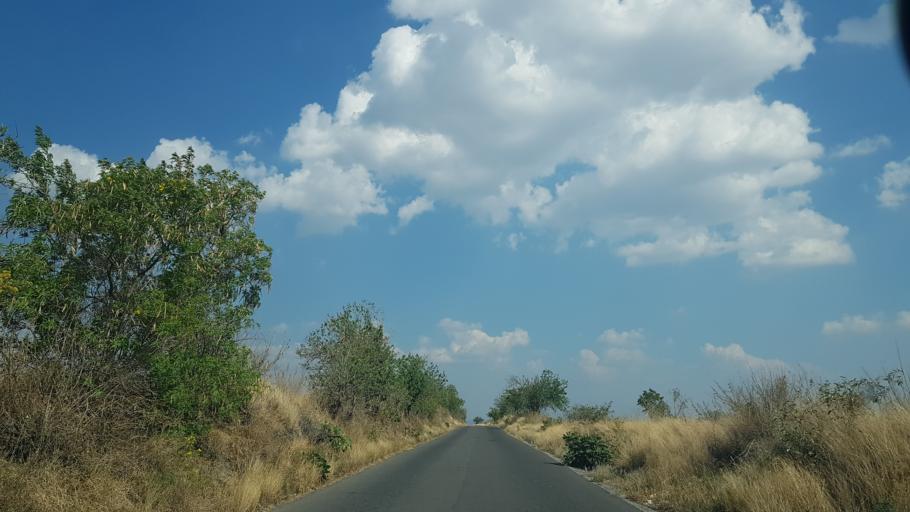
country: MX
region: Puebla
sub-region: Atlixco
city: Colonia Agricola de Ocotepec (Colonia San Jose)
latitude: 18.9202
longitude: -98.5322
